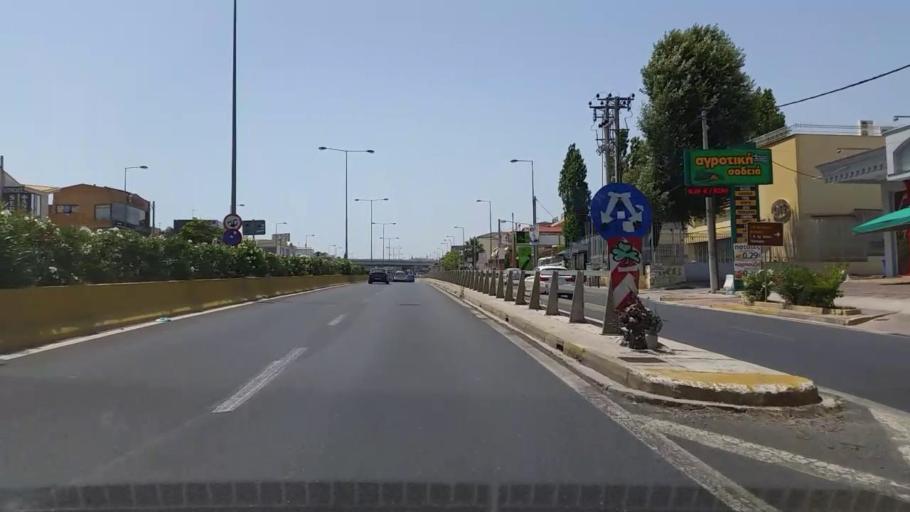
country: GR
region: Attica
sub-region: Nomarchia Anatolikis Attikis
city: Gerakas
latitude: 38.0098
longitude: 23.8492
